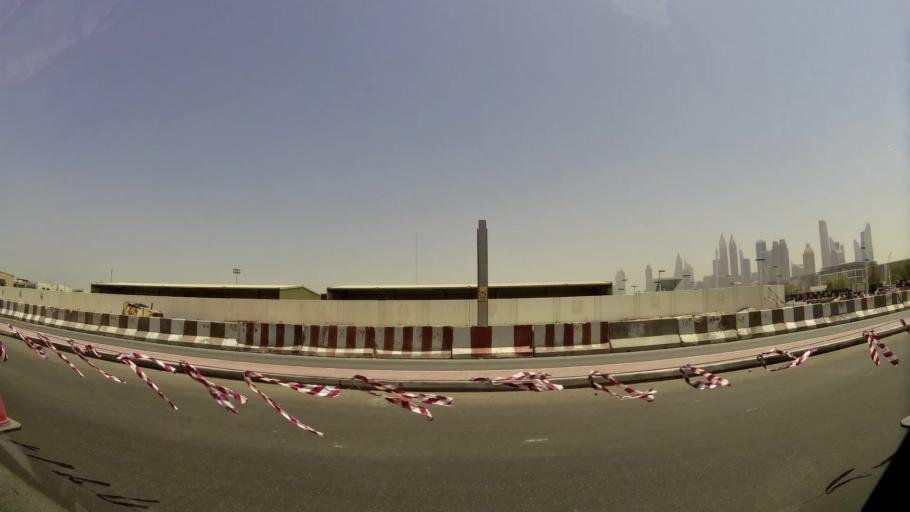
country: AE
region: Dubai
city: Dubai
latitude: 25.2040
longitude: 55.2566
